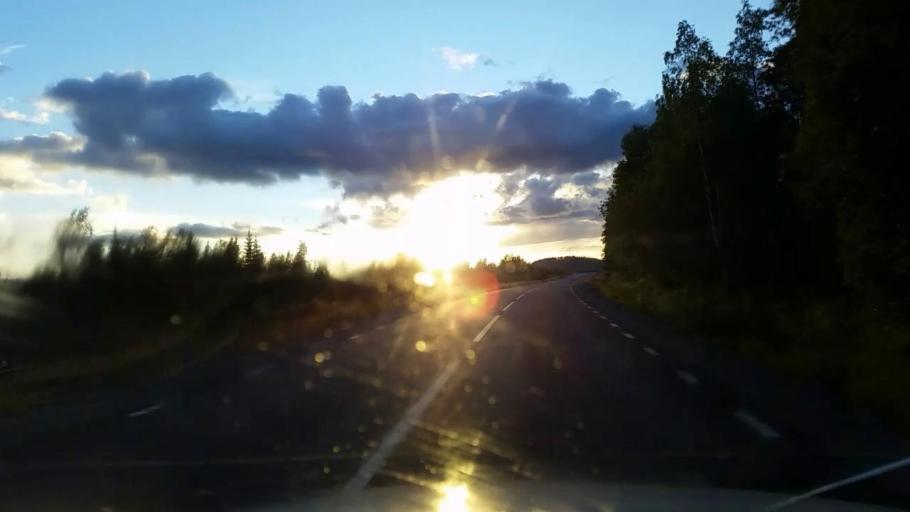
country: SE
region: Gaevleborg
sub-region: Ljusdals Kommun
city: Farila
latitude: 62.1321
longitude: 15.6978
